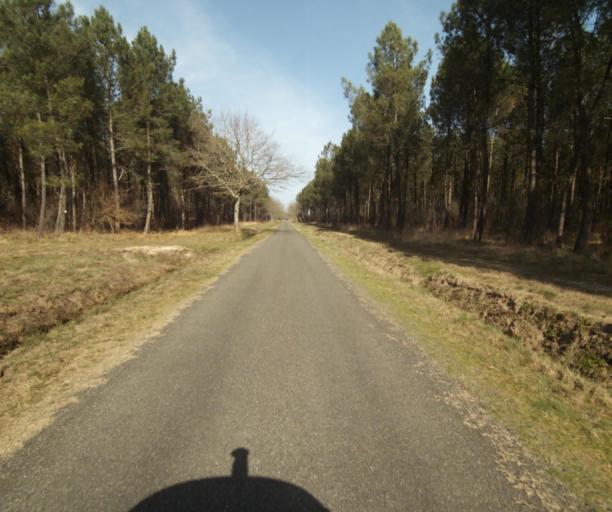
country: FR
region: Aquitaine
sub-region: Departement de la Gironde
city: Bazas
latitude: 44.2208
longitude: -0.2049
